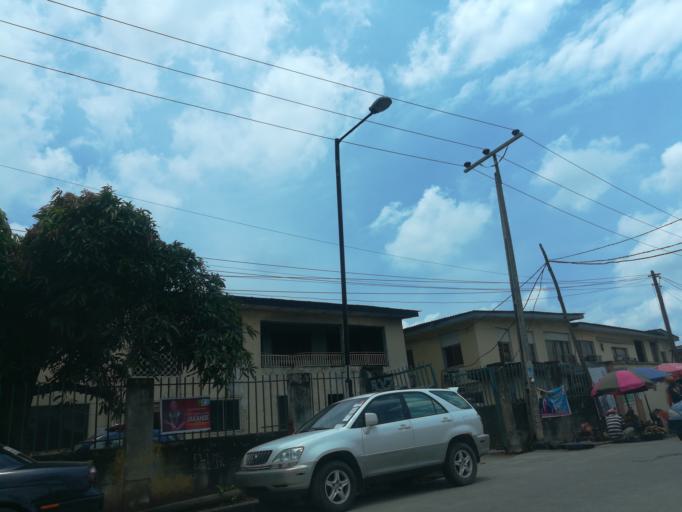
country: NG
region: Lagos
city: Somolu
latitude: 6.5487
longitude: 3.3616
